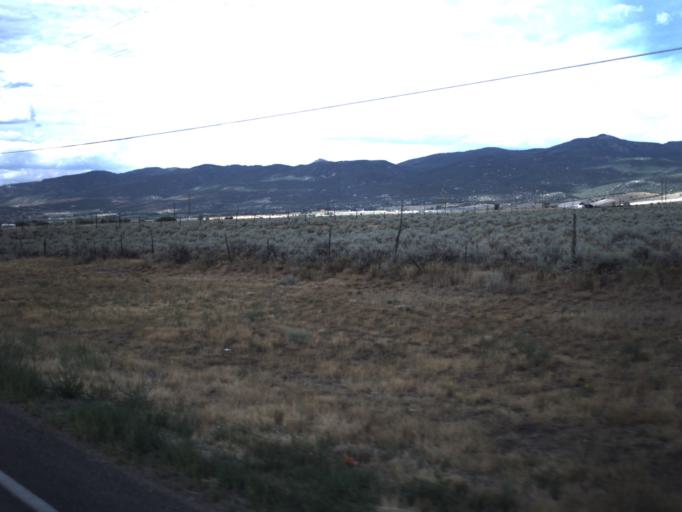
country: US
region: Utah
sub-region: Sanpete County
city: Mount Pleasant
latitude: 39.5583
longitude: -111.4554
